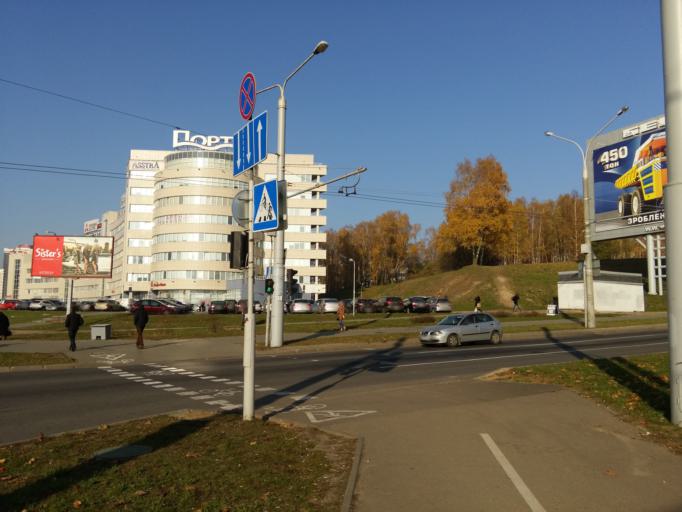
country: BY
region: Minsk
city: Borovlyany
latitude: 53.9444
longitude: 27.6837
